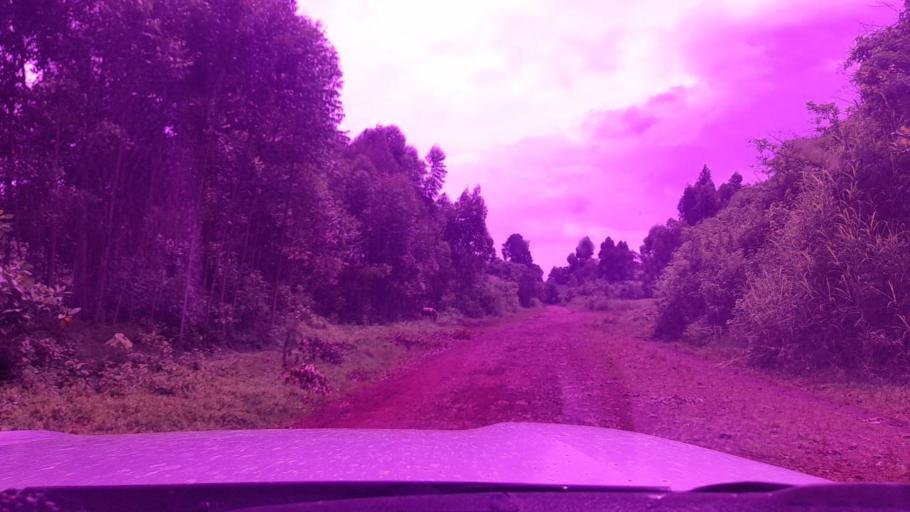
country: ET
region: Southern Nations, Nationalities, and People's Region
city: Tippi
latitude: 7.6268
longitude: 35.5578
